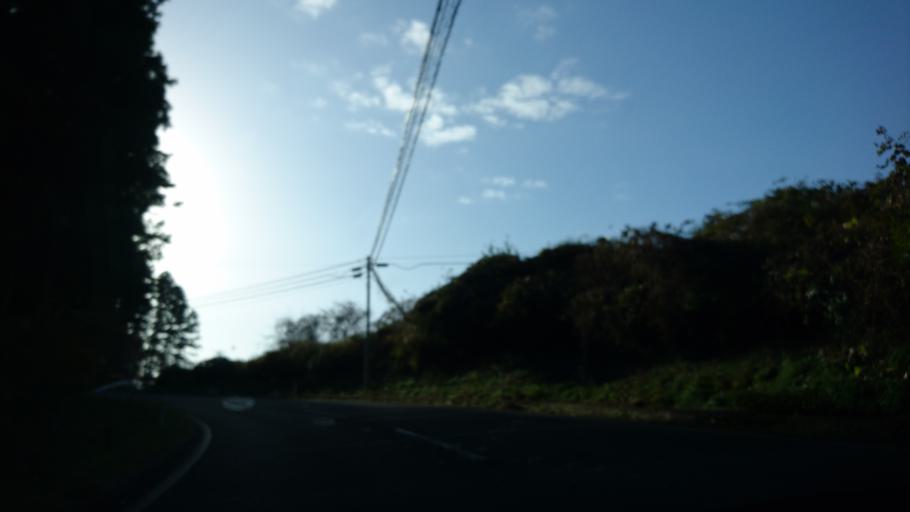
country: JP
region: Iwate
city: Ichinoseki
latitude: 38.8896
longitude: 141.2843
